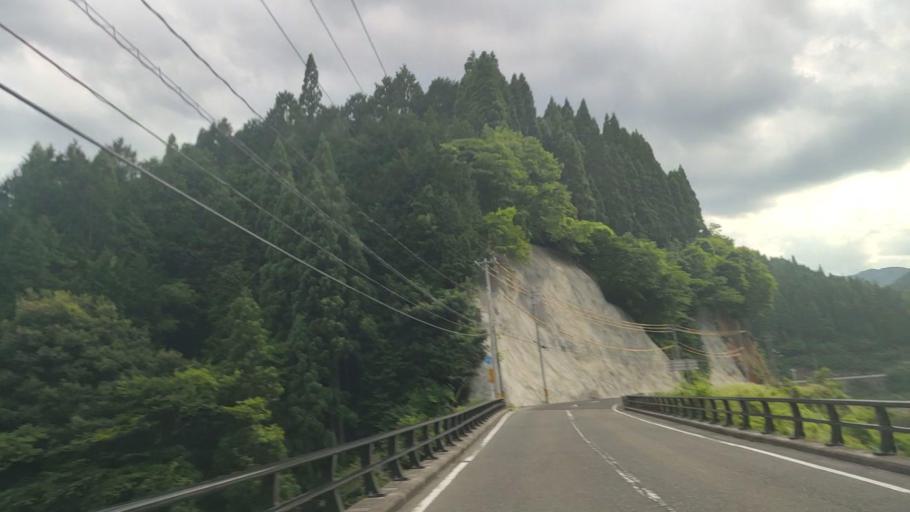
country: JP
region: Tottori
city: Kurayoshi
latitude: 35.3274
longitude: 134.0416
